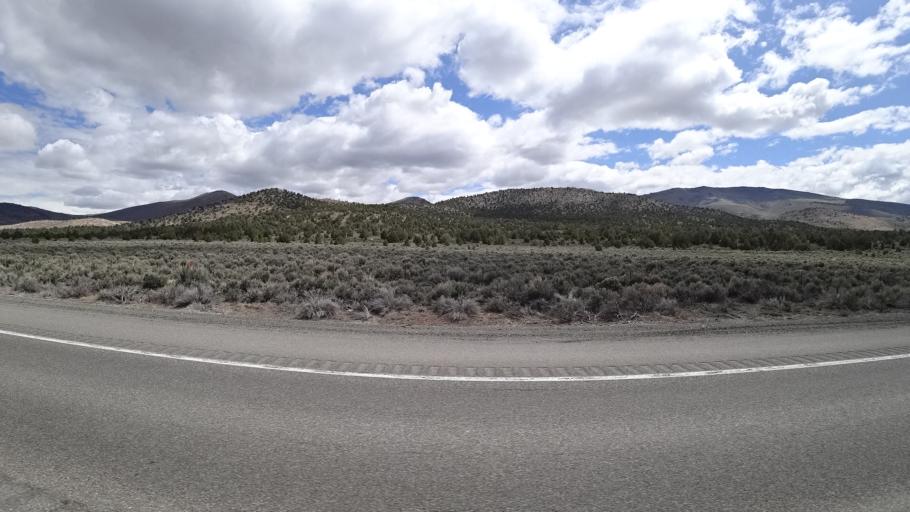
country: US
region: Nevada
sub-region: Douglas County
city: Gardnerville Ranchos
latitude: 38.7978
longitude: -119.6027
